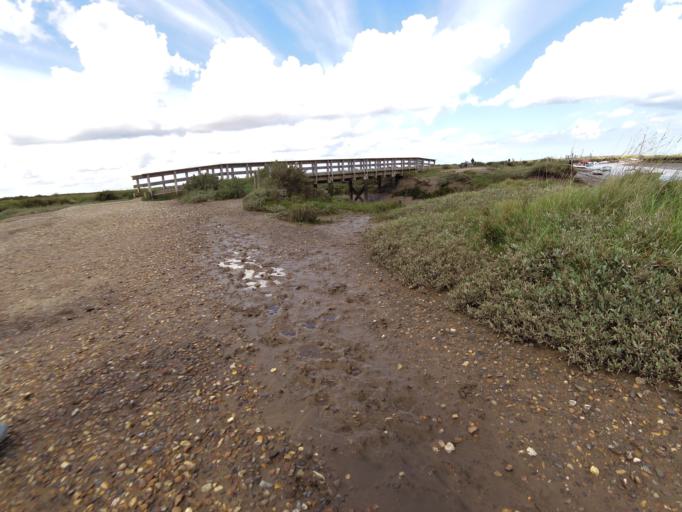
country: GB
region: England
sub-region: Norfolk
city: Briston
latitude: 52.9592
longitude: 0.9836
